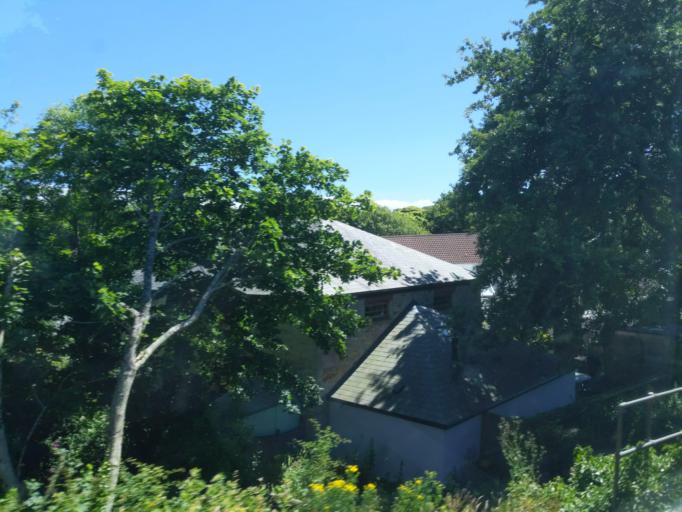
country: GB
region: England
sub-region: Cornwall
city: St. Day
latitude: 50.2544
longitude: -5.1943
